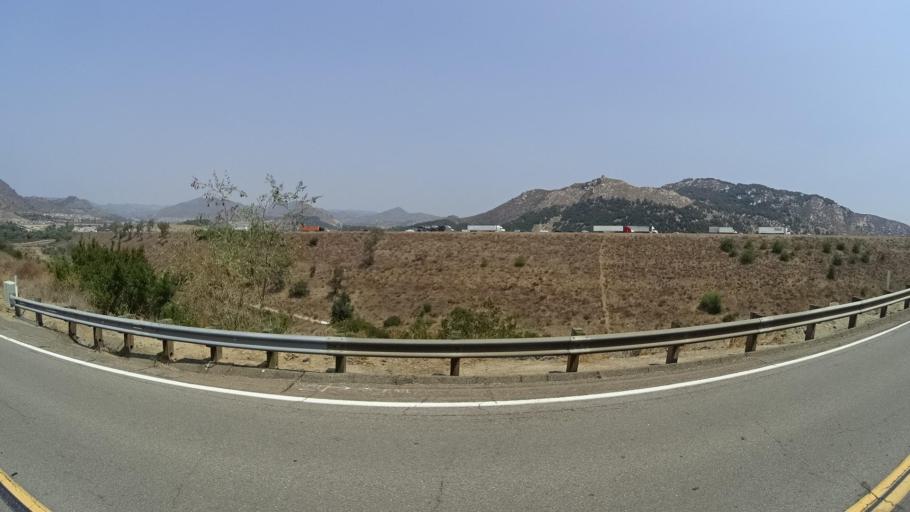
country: US
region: California
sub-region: San Diego County
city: Bonsall
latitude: 33.3154
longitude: -117.1565
